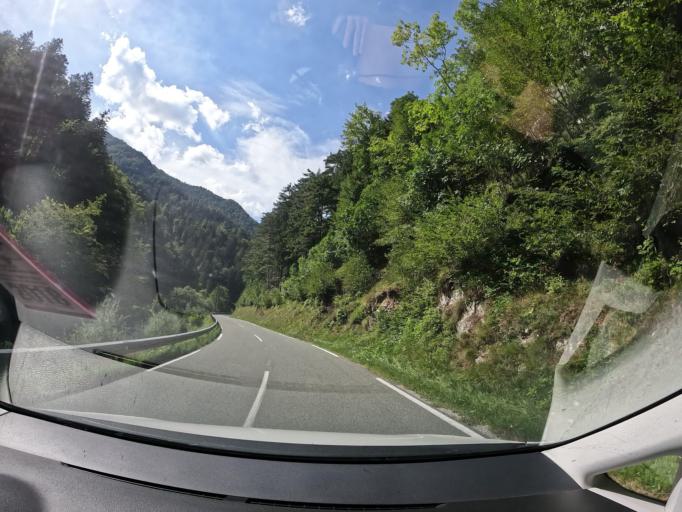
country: SI
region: Jezersko
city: Zgornje Jezersko
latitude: 46.3638
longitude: 14.4526
